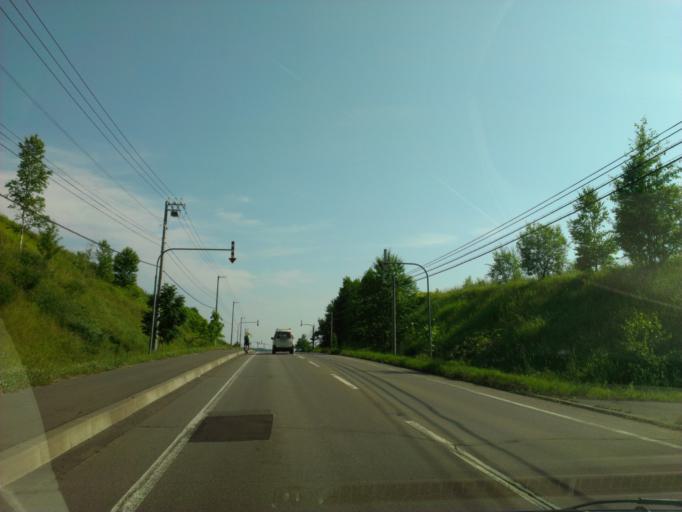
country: JP
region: Hokkaido
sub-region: Asahikawa-shi
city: Asahikawa
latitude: 43.6053
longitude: 142.4767
